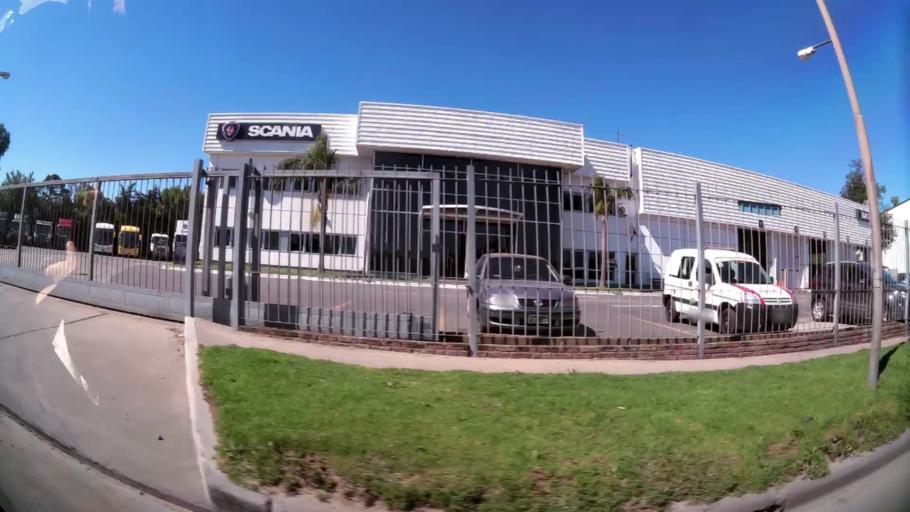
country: AR
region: Buenos Aires
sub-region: Partido de Tigre
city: Tigre
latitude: -34.4836
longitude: -58.6296
